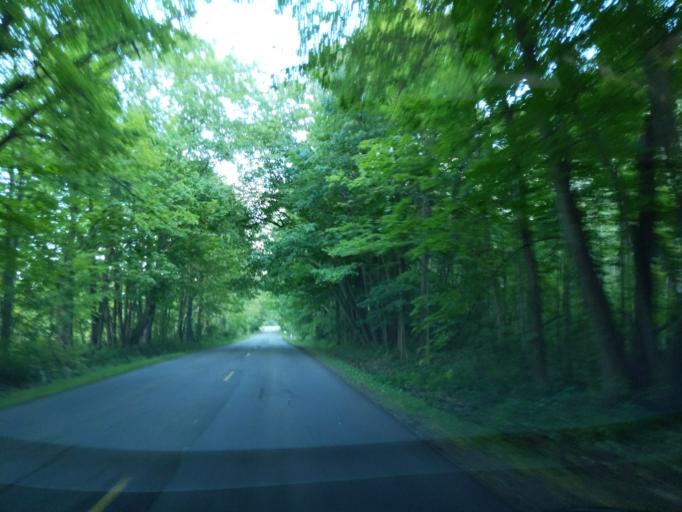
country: US
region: Michigan
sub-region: Ingham County
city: Holt
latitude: 42.6112
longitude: -84.5145
